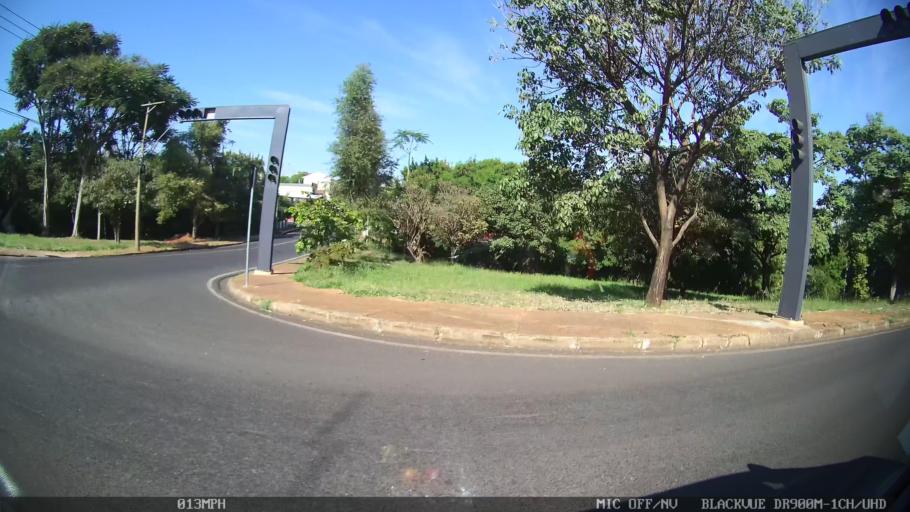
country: BR
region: Sao Paulo
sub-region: Sao Jose Do Rio Preto
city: Sao Jose do Rio Preto
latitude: -20.7860
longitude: -49.3739
